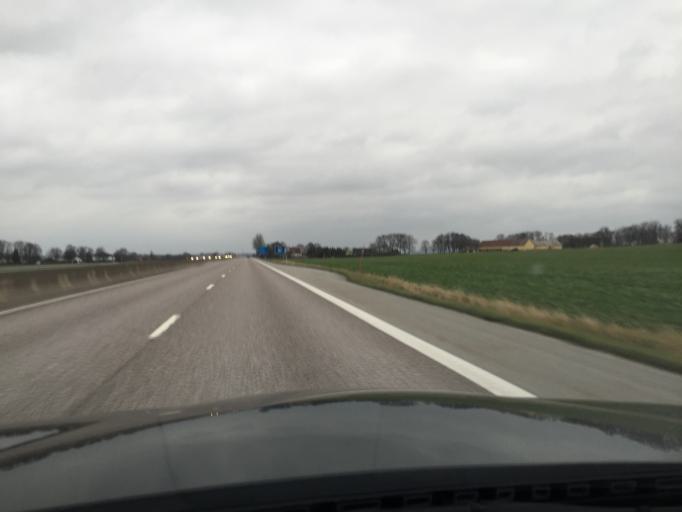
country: SE
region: Skane
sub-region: Staffanstorps Kommun
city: Hjaerup
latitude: 55.6669
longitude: 13.1620
